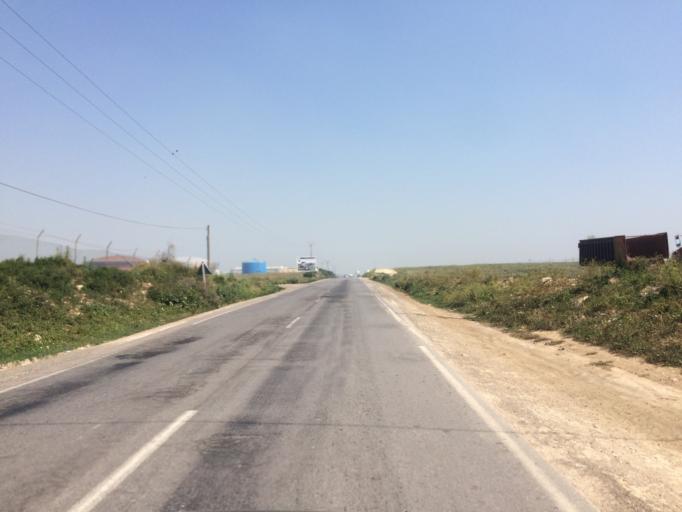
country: MA
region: Doukkala-Abda
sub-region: El-Jadida
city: Moulay Abdallah
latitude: 33.1477
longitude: -8.6066
